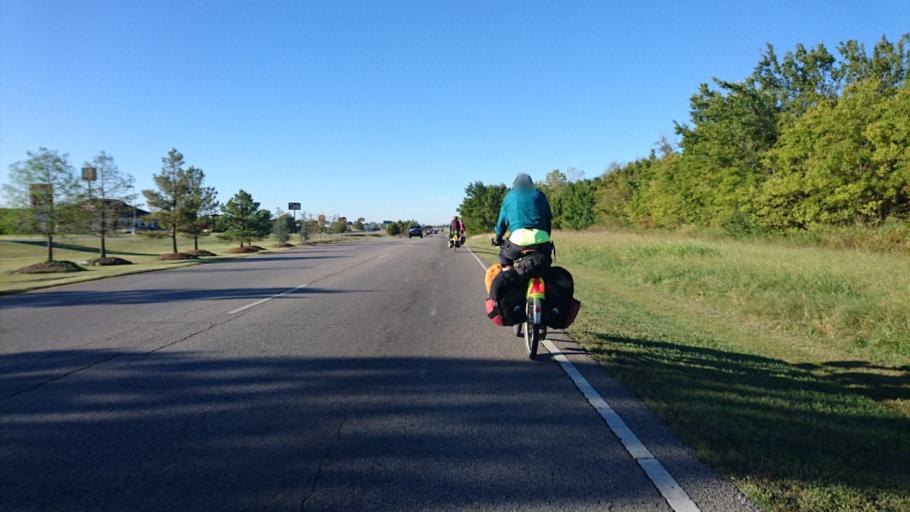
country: US
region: Oklahoma
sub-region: Rogers County
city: Claremore
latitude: 36.2893
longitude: -95.6337
